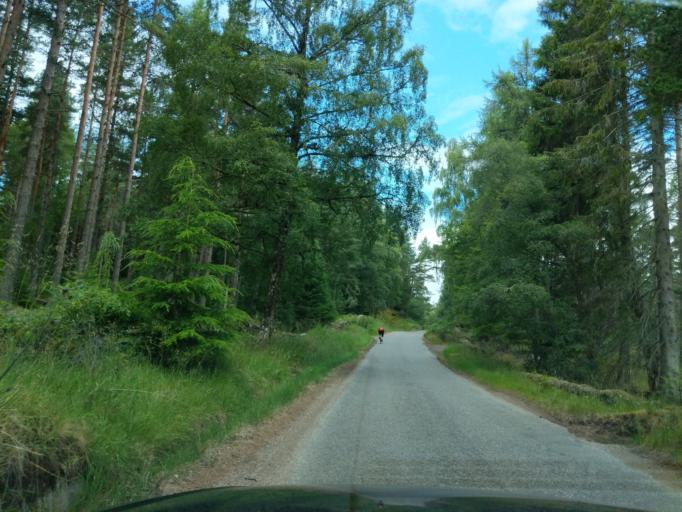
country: GB
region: Scotland
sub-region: Aberdeenshire
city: Ballater
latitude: 57.0400
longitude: -3.0760
